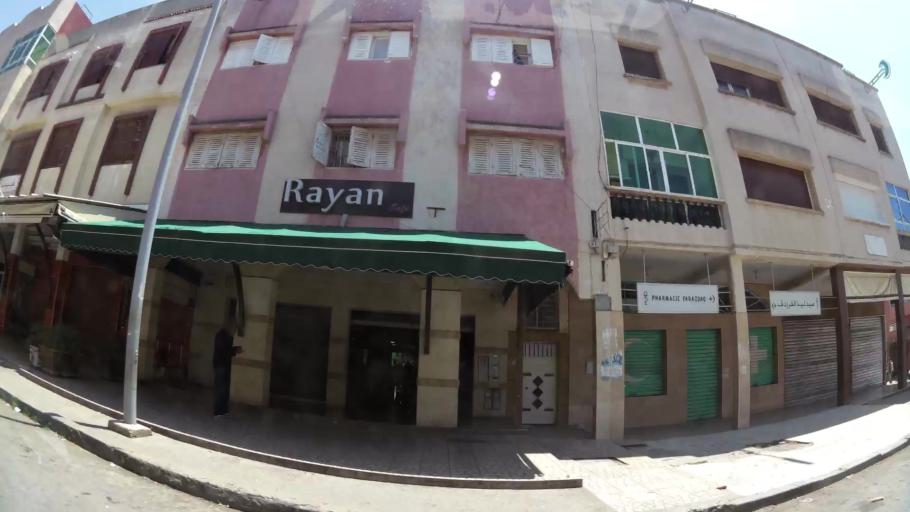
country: MA
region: Gharb-Chrarda-Beni Hssen
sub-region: Kenitra Province
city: Kenitra
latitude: 34.2568
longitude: -6.6222
